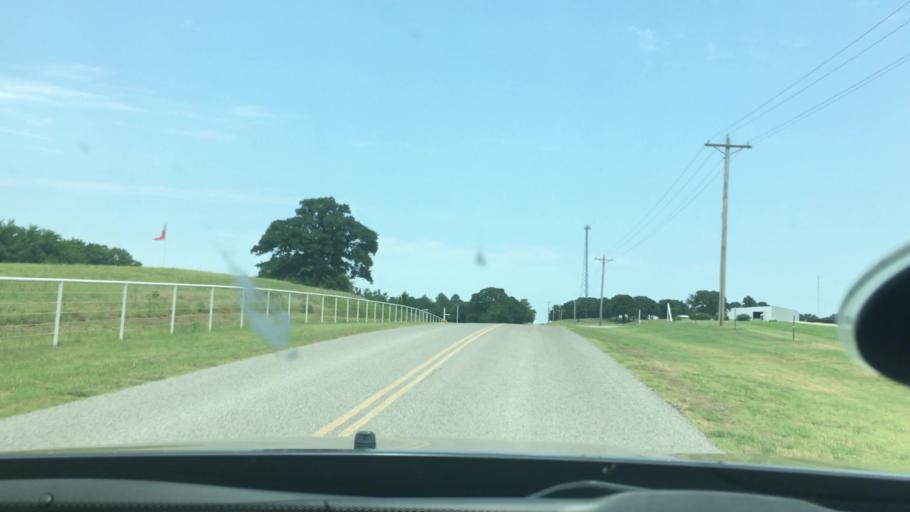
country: US
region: Oklahoma
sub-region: Love County
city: Marietta
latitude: 33.9336
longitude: -97.3522
